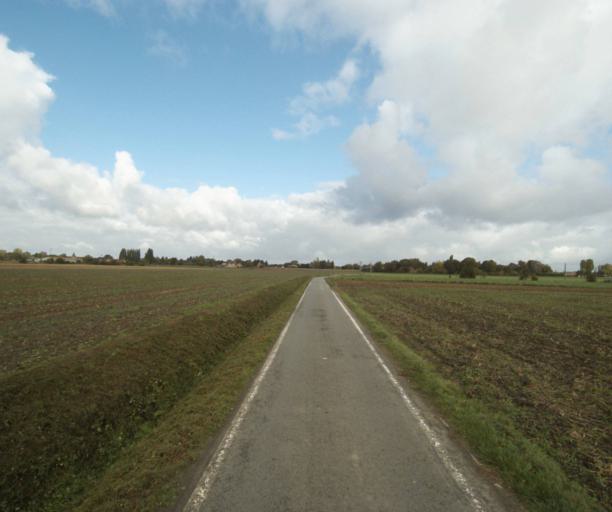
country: FR
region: Nord-Pas-de-Calais
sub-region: Departement du Nord
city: Verlinghem
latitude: 50.6729
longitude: 3.0105
